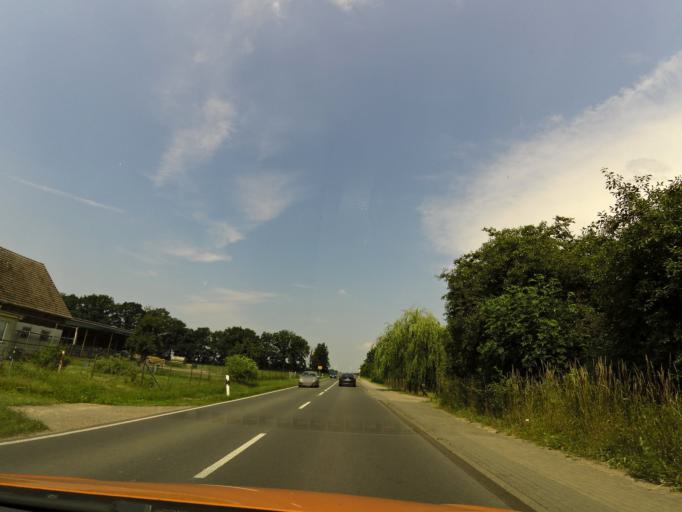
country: DE
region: Brandenburg
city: Pritzwalk
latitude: 53.1956
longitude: 12.1992
